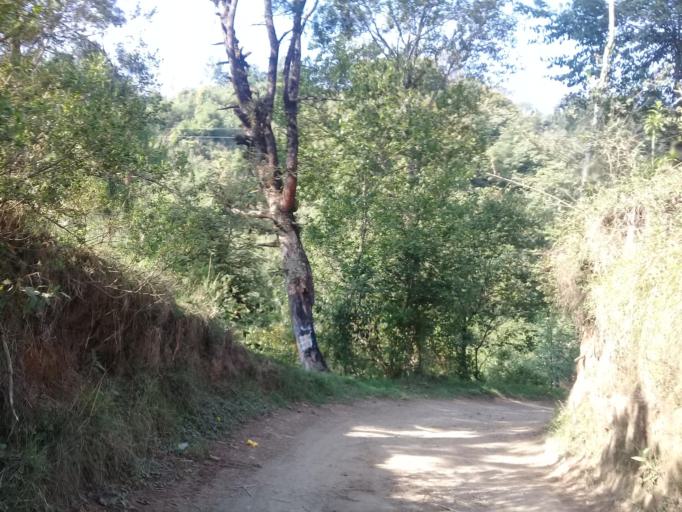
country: MX
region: Veracruz
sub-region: Mariano Escobedo
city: San Isidro el Berro
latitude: 18.9449
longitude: -97.2139
